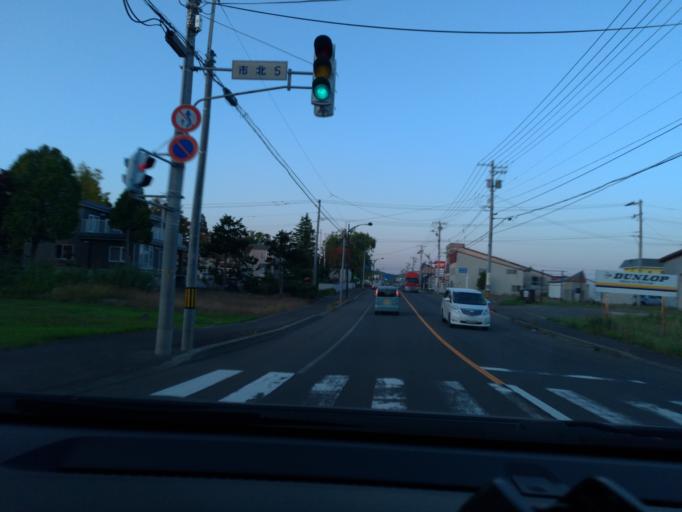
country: JP
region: Hokkaido
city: Iwamizawa
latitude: 43.3365
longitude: 141.6719
